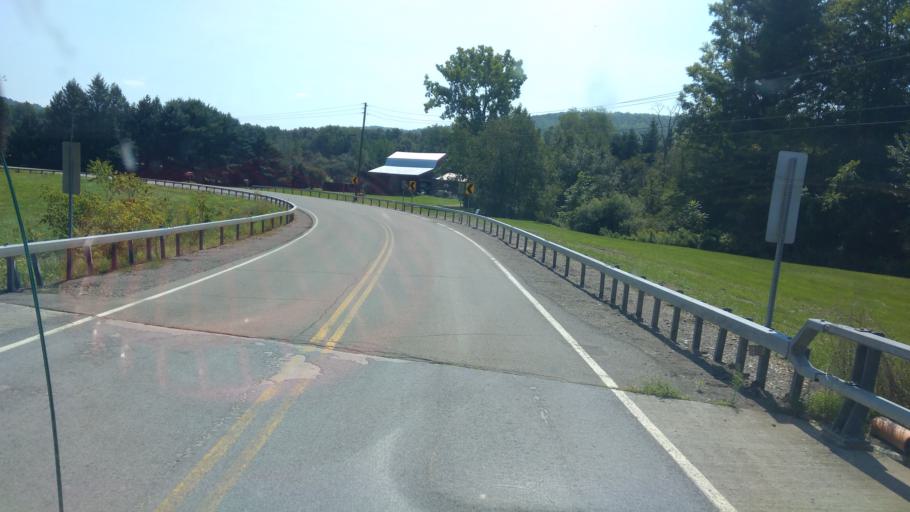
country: US
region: New York
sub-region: Allegany County
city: Belmont
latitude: 42.3010
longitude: -77.9876
